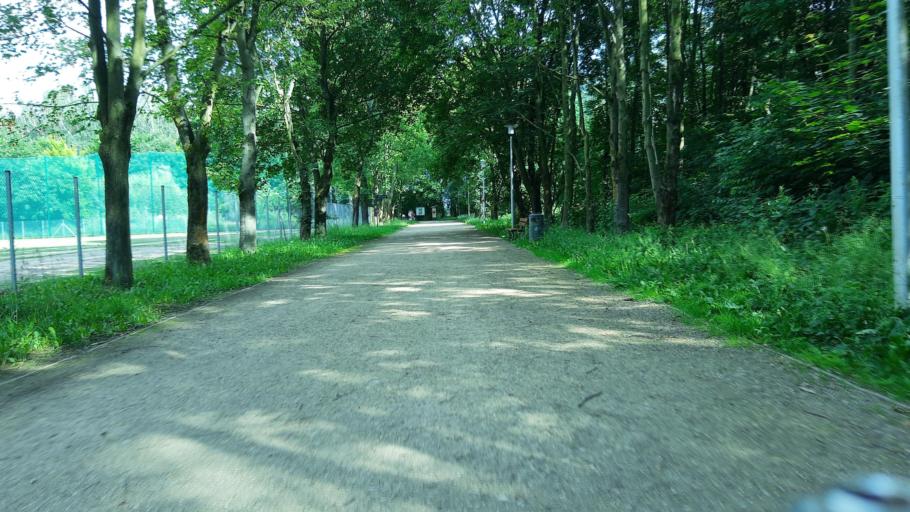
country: PL
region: Lodz Voivodeship
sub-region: Powiat sieradzki
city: Sieradz
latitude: 51.5959
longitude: 18.7546
